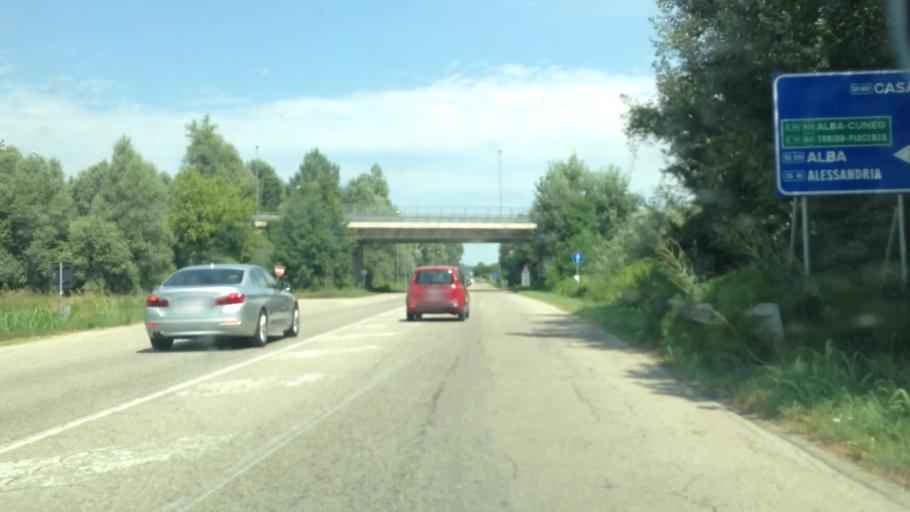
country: IT
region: Piedmont
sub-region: Provincia di Asti
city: Asti
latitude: 44.9230
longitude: 8.2262
